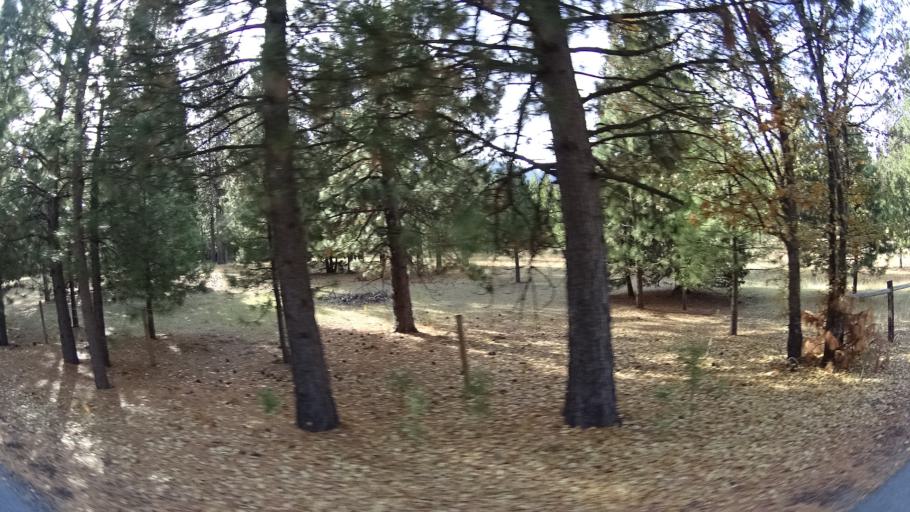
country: US
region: California
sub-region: Siskiyou County
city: Weed
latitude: 41.3931
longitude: -122.4131
